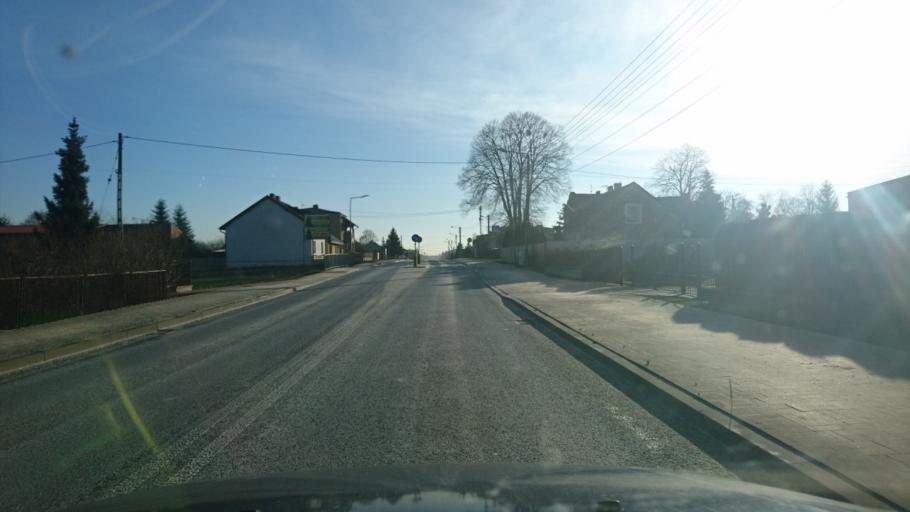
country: PL
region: Silesian Voivodeship
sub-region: Powiat klobucki
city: Starokrzepice
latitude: 51.0156
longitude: 18.6541
